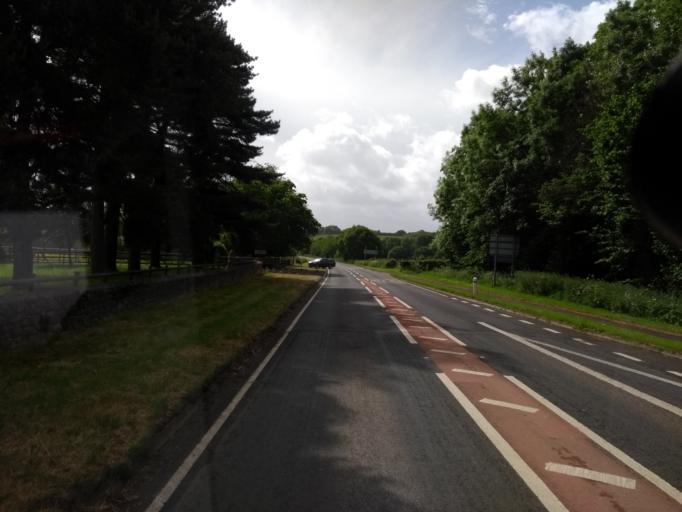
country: GB
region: England
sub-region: Somerset
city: Bishops Lydeard
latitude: 51.1496
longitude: -3.1512
